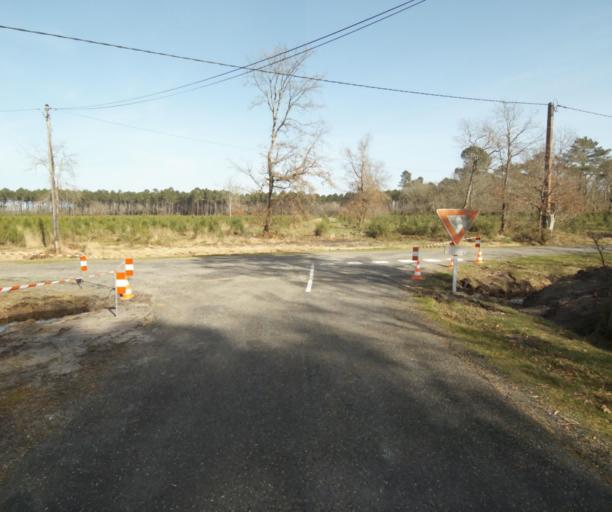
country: FR
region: Aquitaine
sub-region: Departement des Landes
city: Roquefort
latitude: 44.1372
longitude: -0.2008
